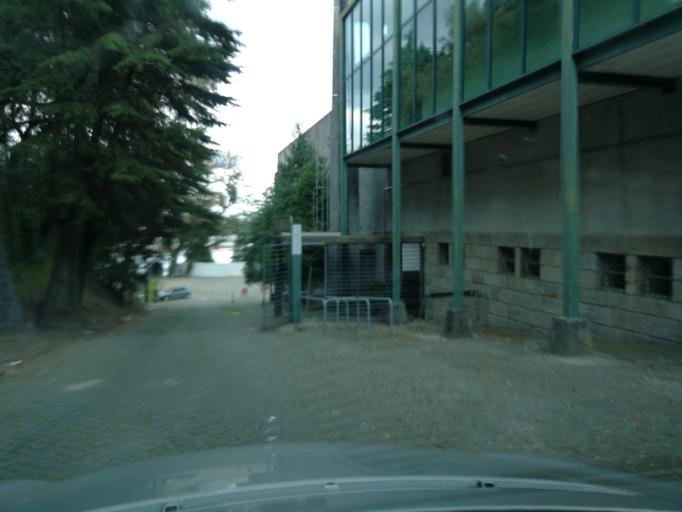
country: PT
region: Braga
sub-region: Braga
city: Braga
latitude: 41.5389
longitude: -8.4216
